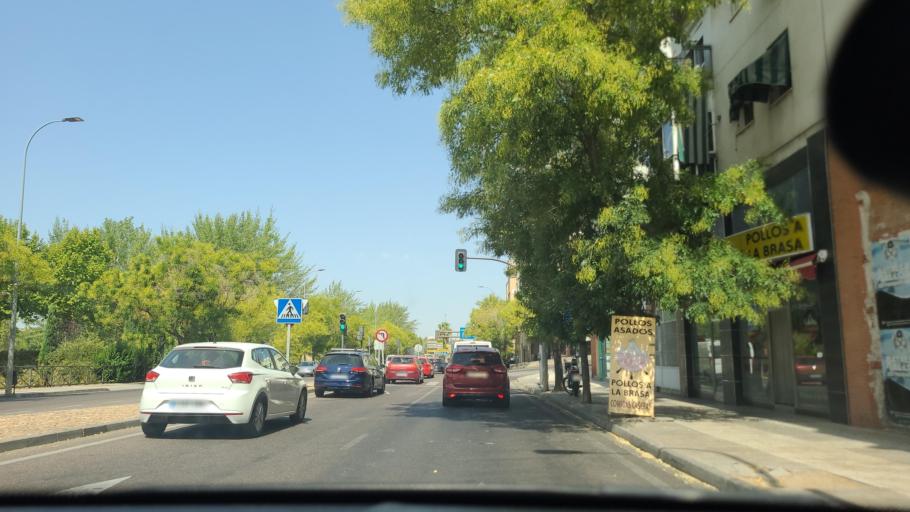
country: ES
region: Extremadura
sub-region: Provincia de Badajoz
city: Badajoz
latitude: 38.8714
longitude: -6.9586
